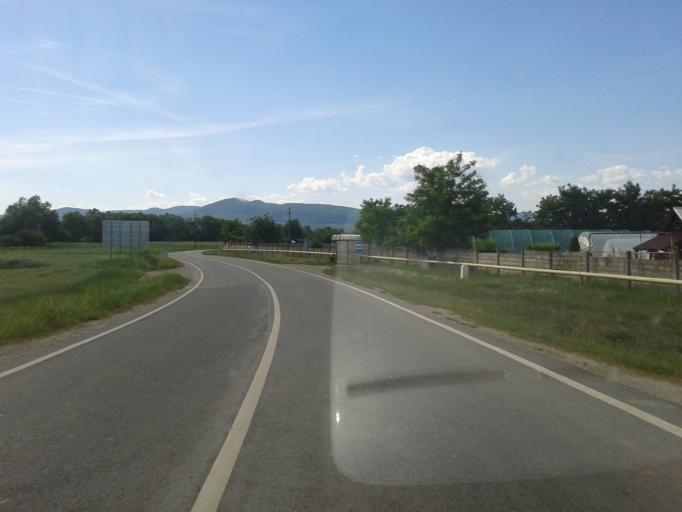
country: RO
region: Hunedoara
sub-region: Comuna Geoagiu
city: Geoagiu
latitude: 45.8882
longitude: 23.2385
